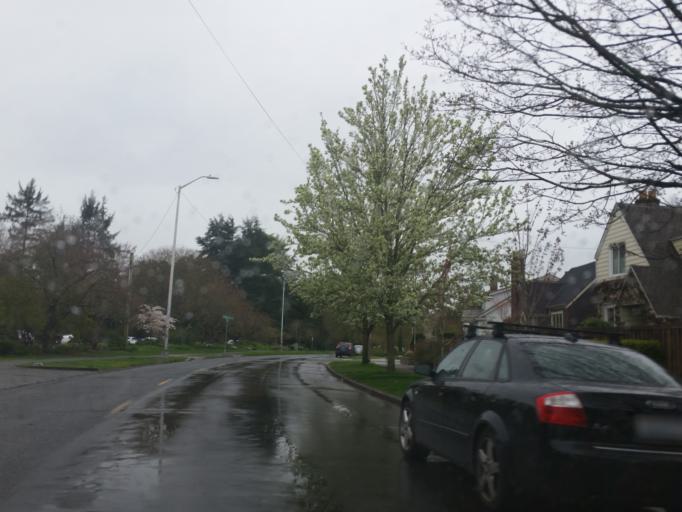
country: US
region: Washington
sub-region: King County
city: Shoreline
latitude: 47.6826
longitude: -122.3409
